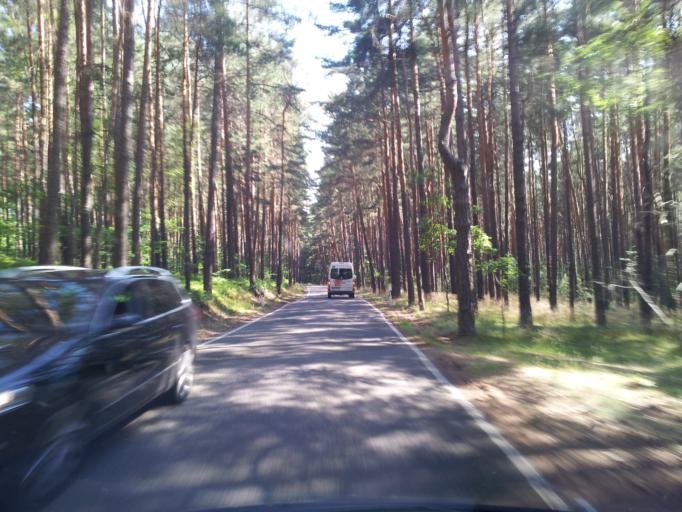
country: DE
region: Saxony
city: Hockendorf
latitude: 51.2053
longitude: 13.9013
